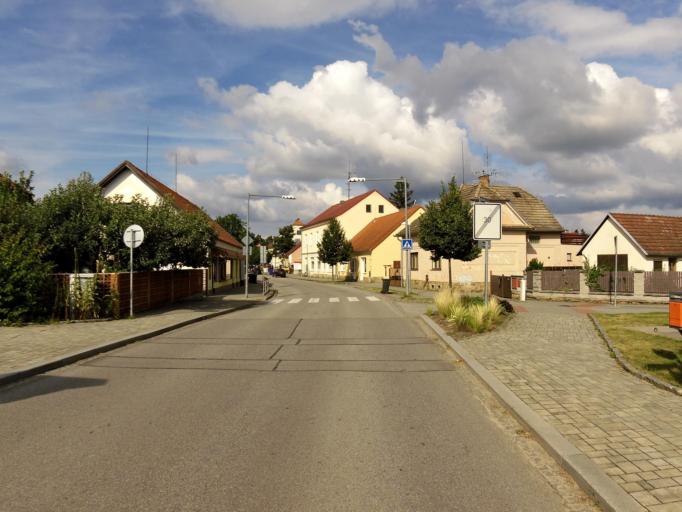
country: CZ
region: Jihocesky
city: Suchdol nad Luznici
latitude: 48.8886
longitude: 14.8752
